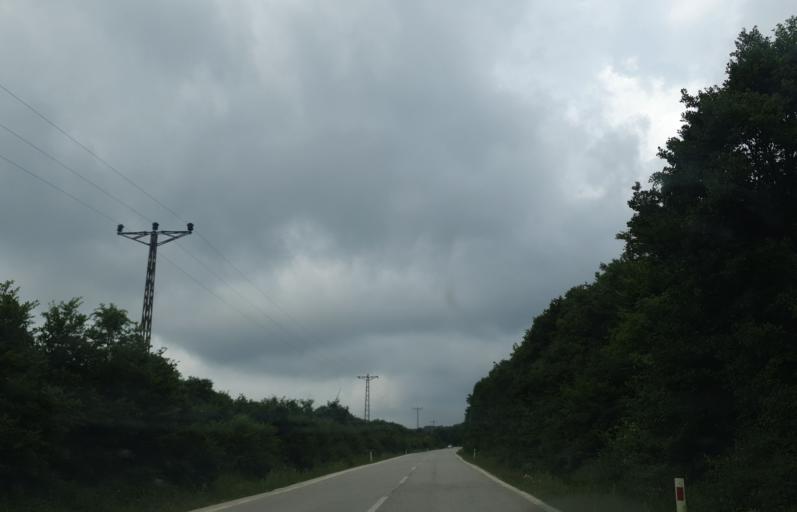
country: TR
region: Tekirdag
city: Saray
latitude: 41.5006
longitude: 27.9948
